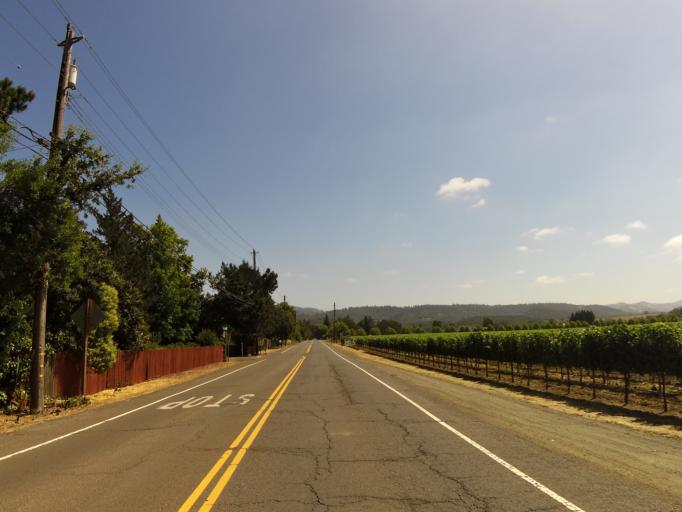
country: US
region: California
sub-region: Napa County
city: Saint Helena
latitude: 38.4837
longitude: -122.4410
